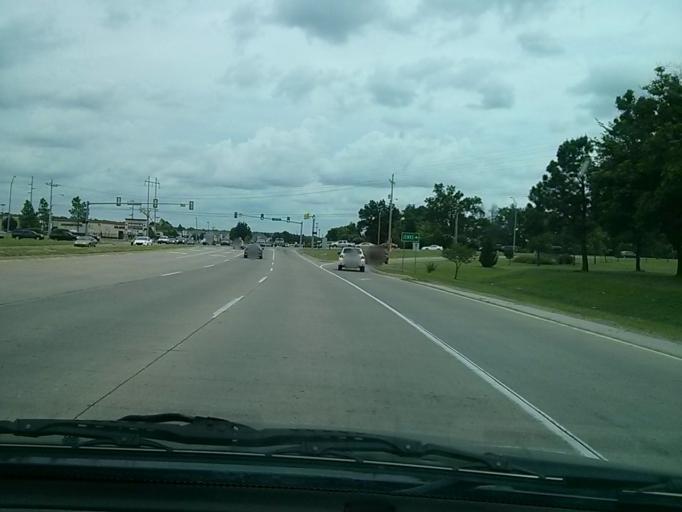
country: US
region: Oklahoma
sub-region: Tulsa County
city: Jenks
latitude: 36.0267
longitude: -95.9513
